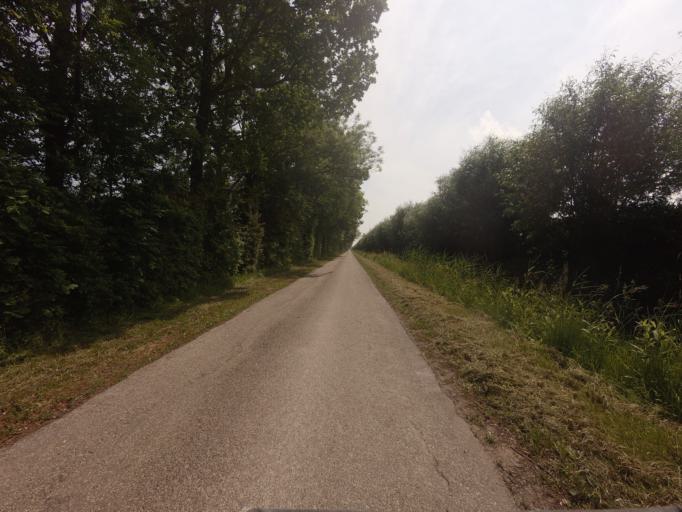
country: NL
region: Gelderland
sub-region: Gemeente Culemborg
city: Culemborg
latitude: 51.9969
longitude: 5.2159
